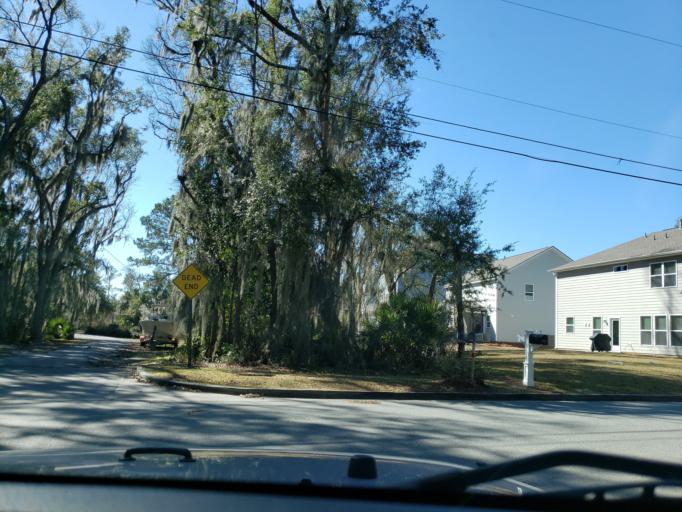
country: US
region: Georgia
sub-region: Chatham County
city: Whitemarsh Island
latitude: 32.0385
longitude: -80.9862
